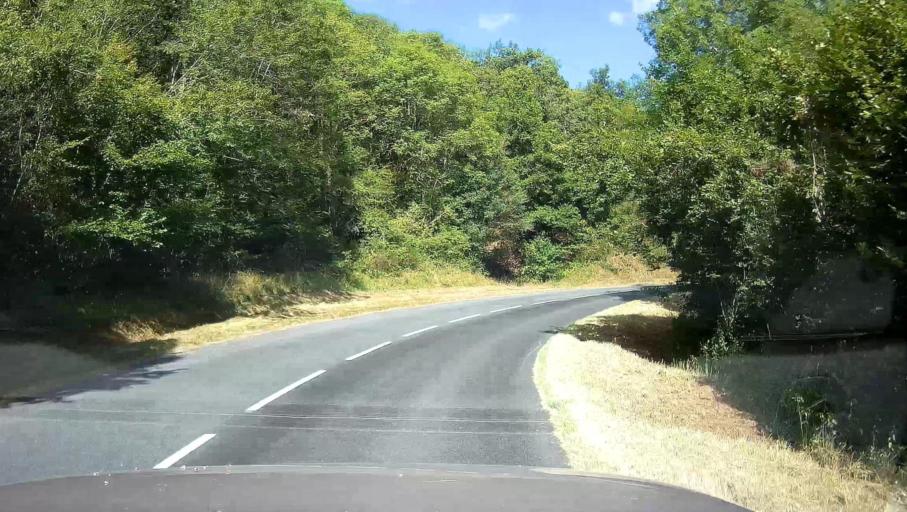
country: FR
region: Rhone-Alpes
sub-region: Departement du Rhone
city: Cogny
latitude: 45.9848
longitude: 4.5778
